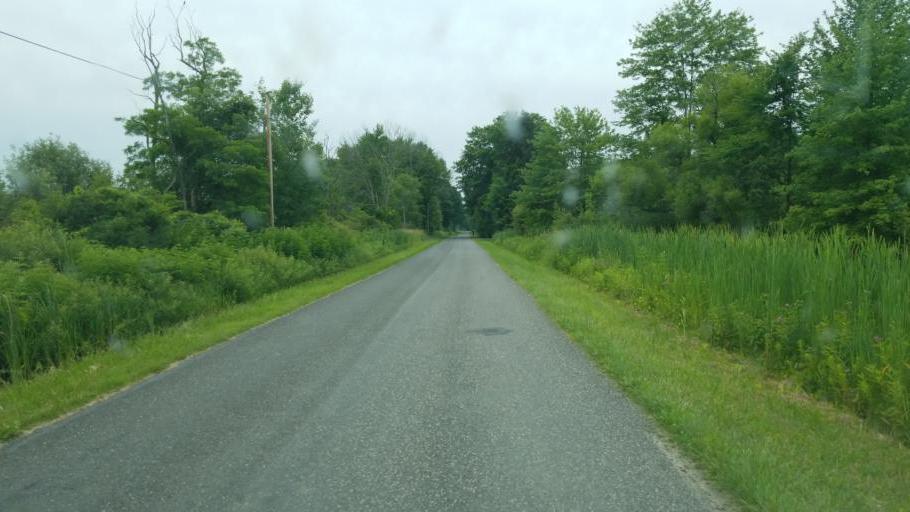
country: US
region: Ohio
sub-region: Ashtabula County
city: Orwell
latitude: 41.4604
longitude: -80.7621
